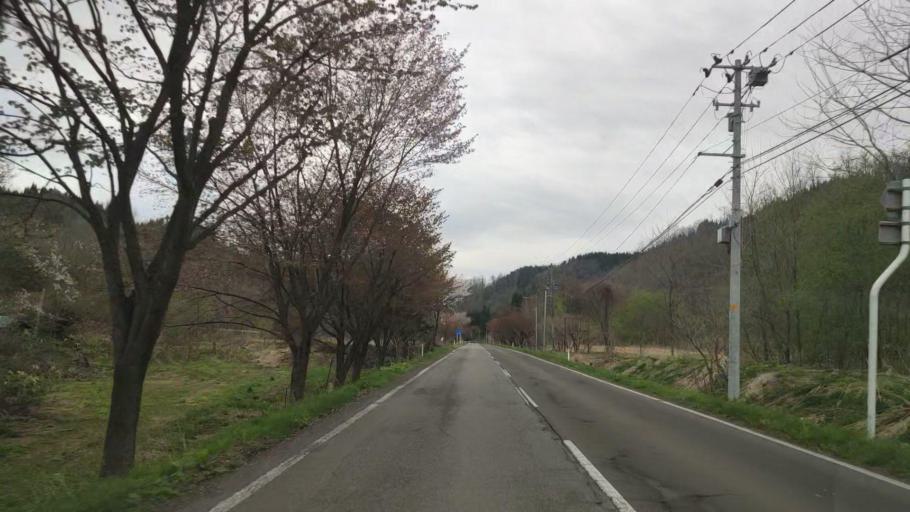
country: JP
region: Akita
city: Hanawa
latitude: 40.3547
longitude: 140.7801
